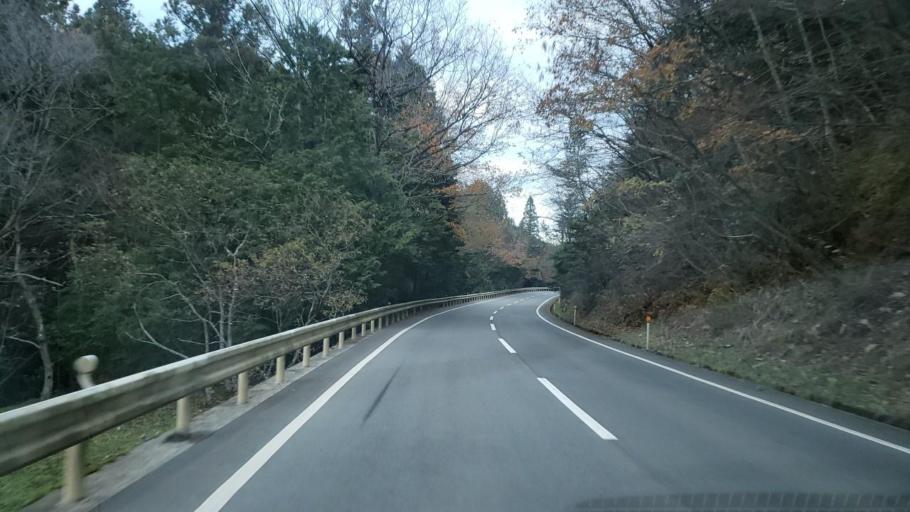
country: JP
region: Tokushima
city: Wakimachi
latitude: 34.1800
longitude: 134.1930
